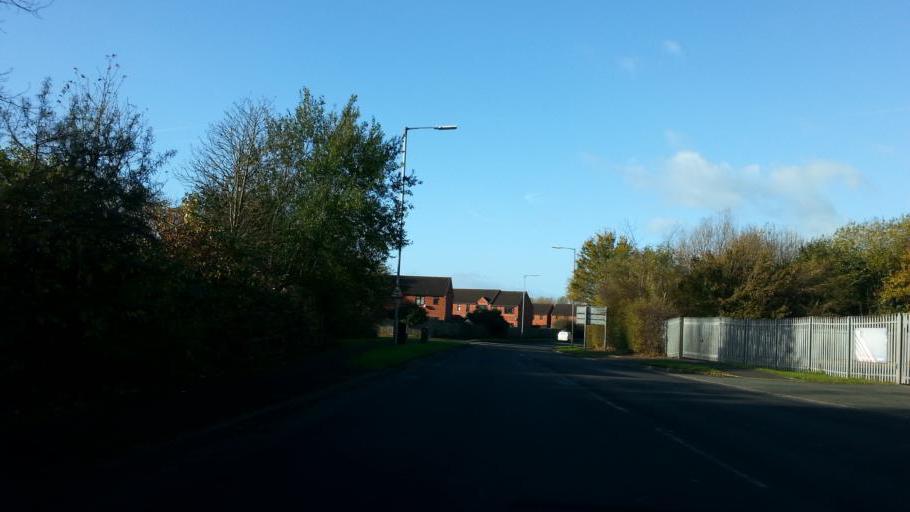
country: GB
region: England
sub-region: Staffordshire
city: Cannock
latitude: 52.6788
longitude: -2.0268
